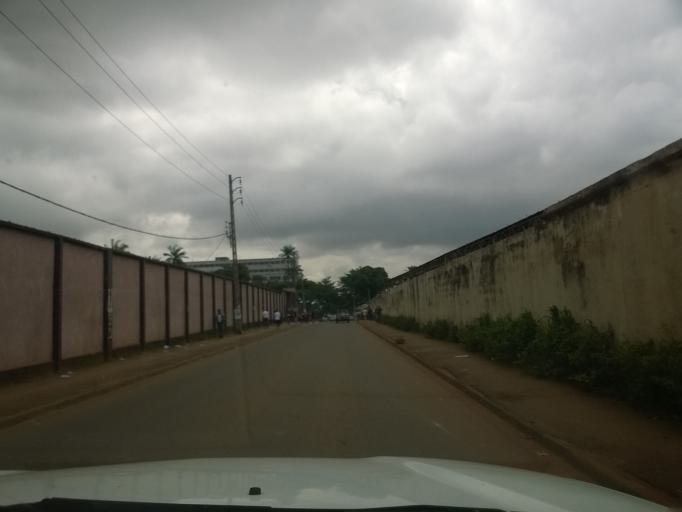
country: CM
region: Centre
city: Yaounde
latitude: 3.8554
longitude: 11.5085
